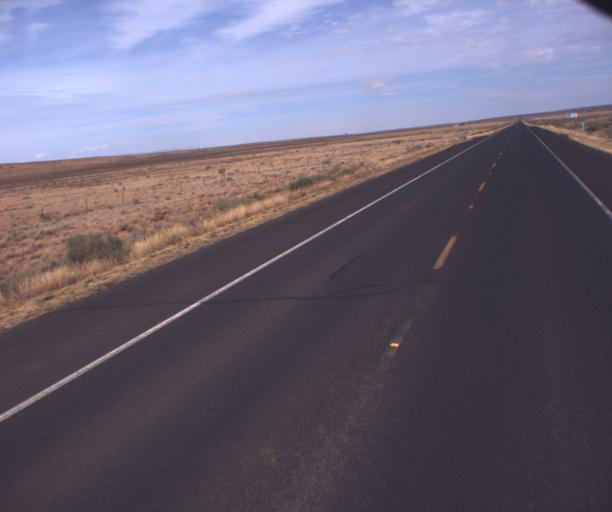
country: US
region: Arizona
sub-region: Apache County
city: Ganado
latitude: 35.7752
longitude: -109.6210
